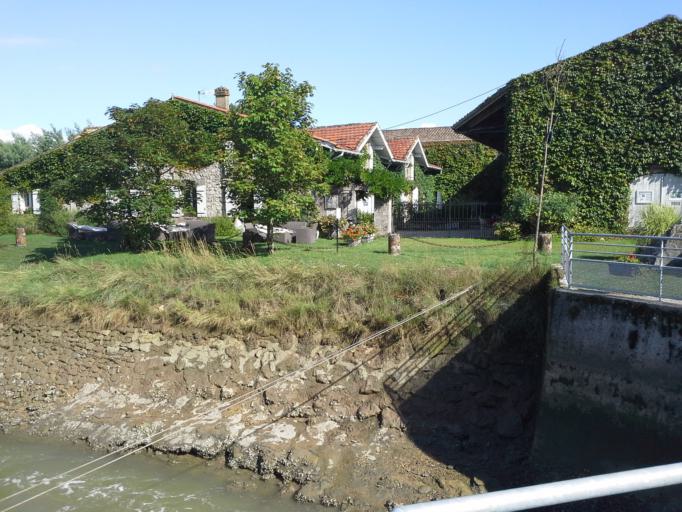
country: FR
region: Aquitaine
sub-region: Departement de la Gironde
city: Gaillan-en-Medoc
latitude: 45.4172
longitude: -0.9274
